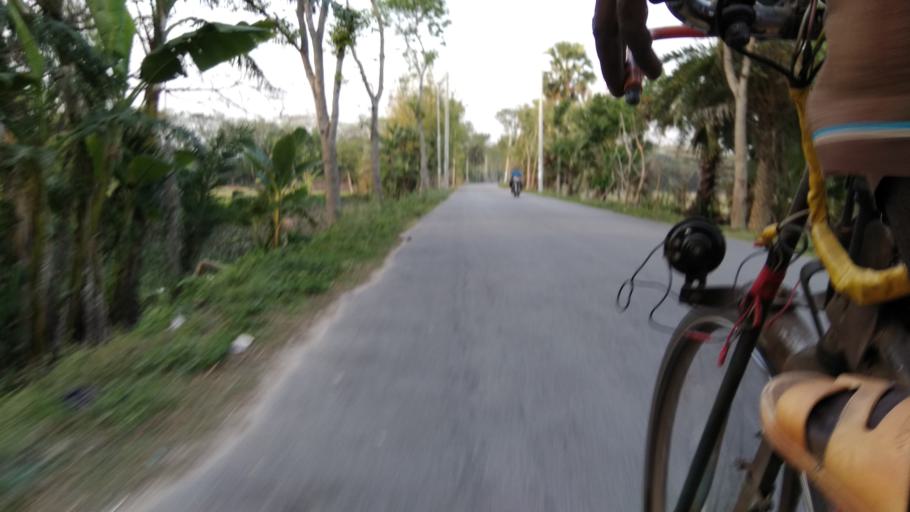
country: BD
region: Barisal
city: Mehendiganj
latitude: 22.9302
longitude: 90.4046
